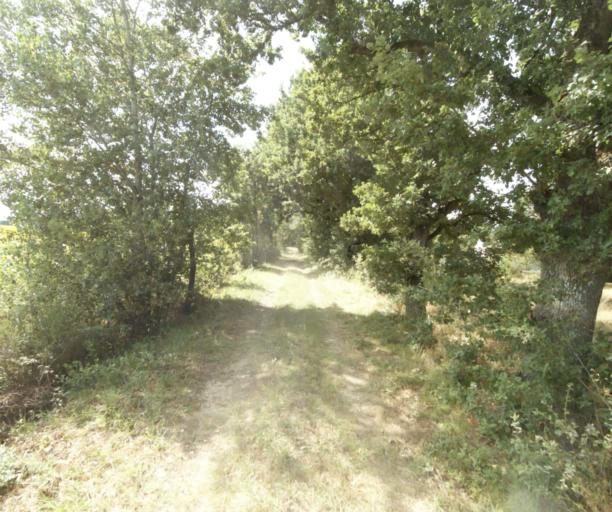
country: FR
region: Midi-Pyrenees
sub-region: Departement du Tarn
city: Soual
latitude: 43.5221
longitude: 2.0852
